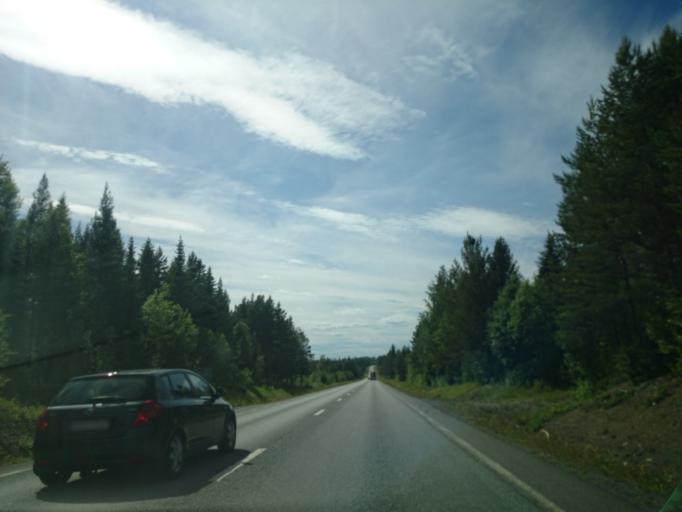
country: SE
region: Jaemtland
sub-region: Krokoms Kommun
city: Krokom
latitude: 63.3235
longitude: 14.2783
